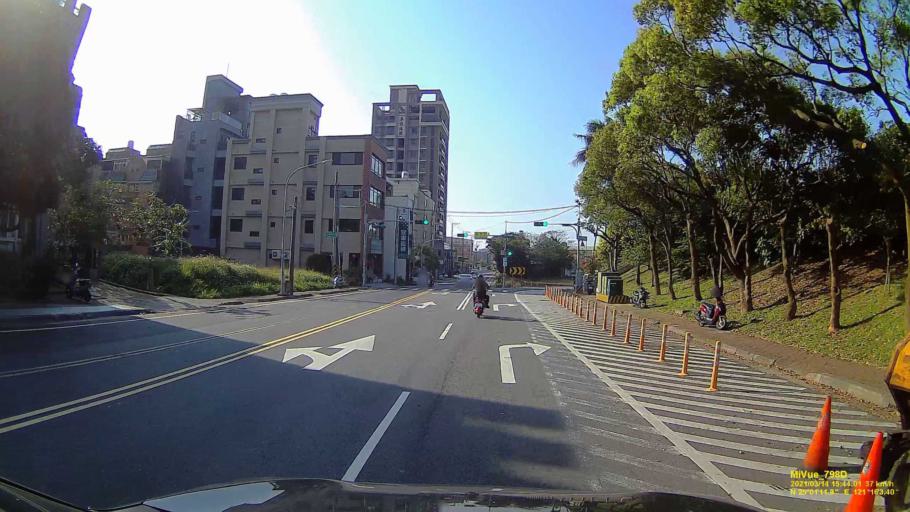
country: TW
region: Taiwan
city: Taoyuan City
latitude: 25.0202
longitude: 121.2674
